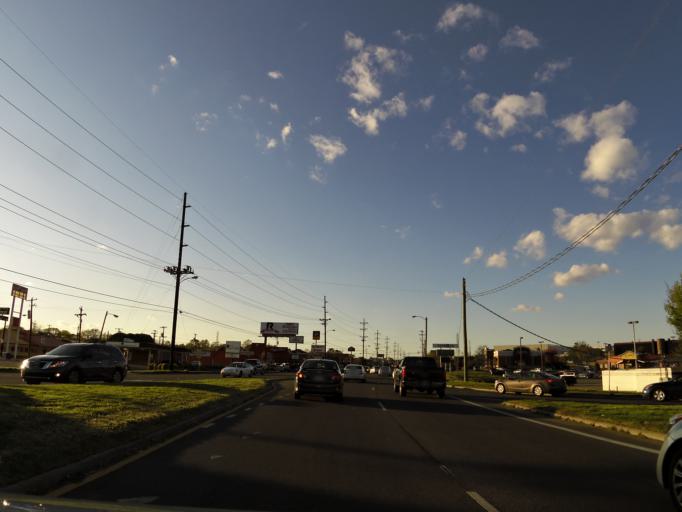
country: US
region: Tennessee
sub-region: Davidson County
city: Goodlettsville
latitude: 36.2972
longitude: -86.6993
